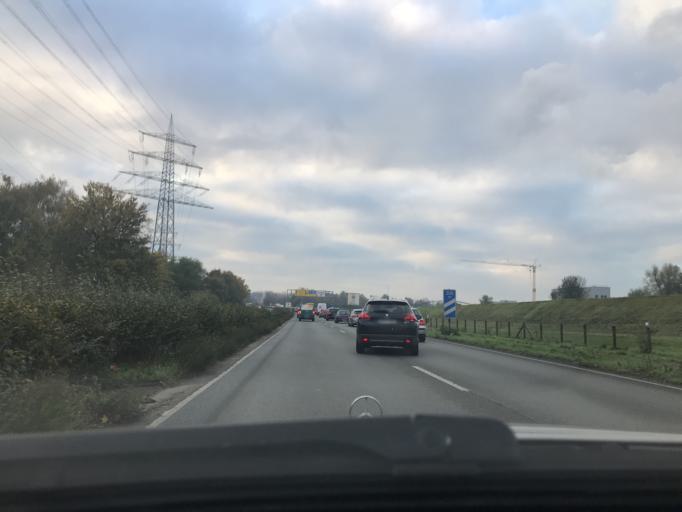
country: DE
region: North Rhine-Westphalia
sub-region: Regierungsbezirk Munster
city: Gladbeck
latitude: 51.5160
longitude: 6.9906
